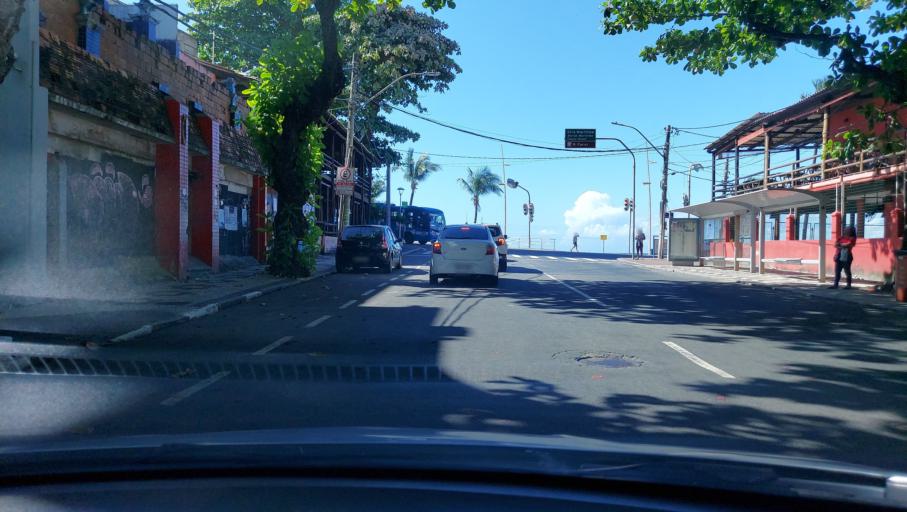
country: BR
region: Bahia
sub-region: Salvador
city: Salvador
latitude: -13.0093
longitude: -38.5243
